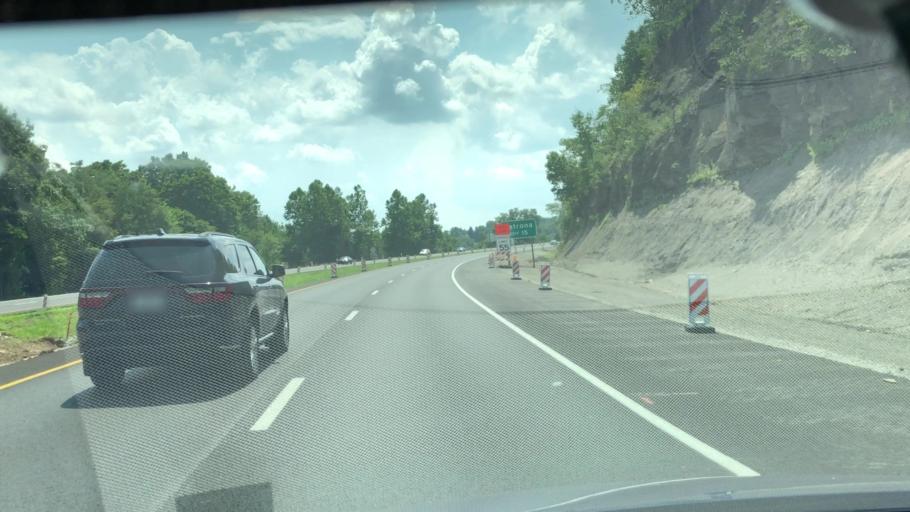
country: US
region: Pennsylvania
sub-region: Allegheny County
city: Brackenridge
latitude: 40.6422
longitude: -79.7203
